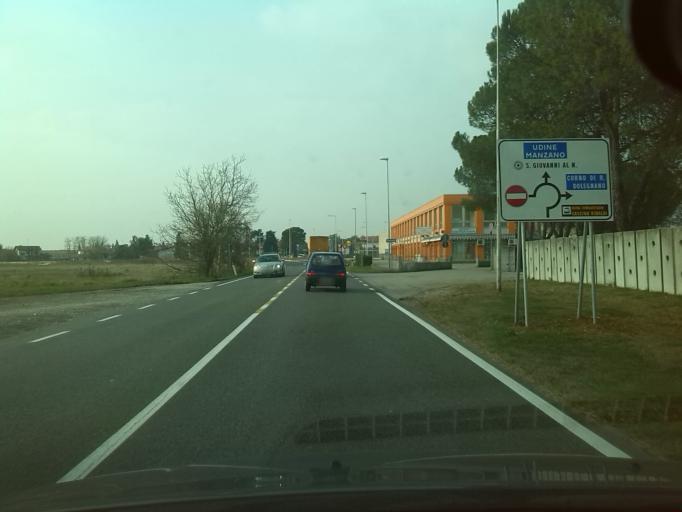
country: IT
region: Friuli Venezia Giulia
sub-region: Provincia di Udine
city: San Giovanni al Natisone
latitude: 45.9697
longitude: 13.4038
